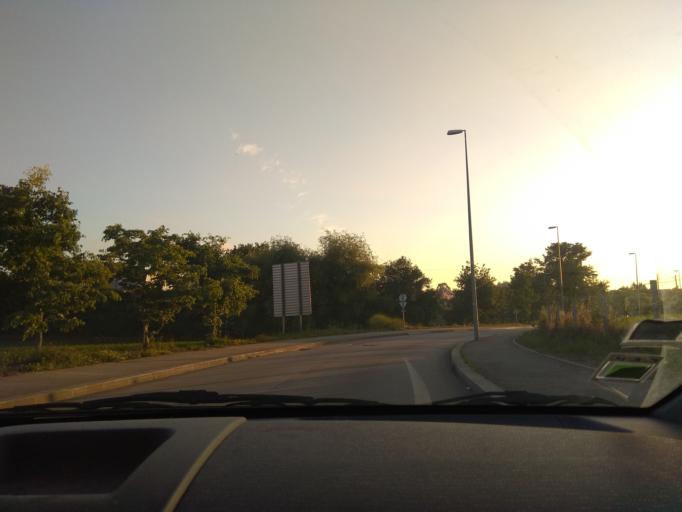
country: PT
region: Porto
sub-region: Matosinhos
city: Senhora da Hora
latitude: 41.2000
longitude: -8.6529
